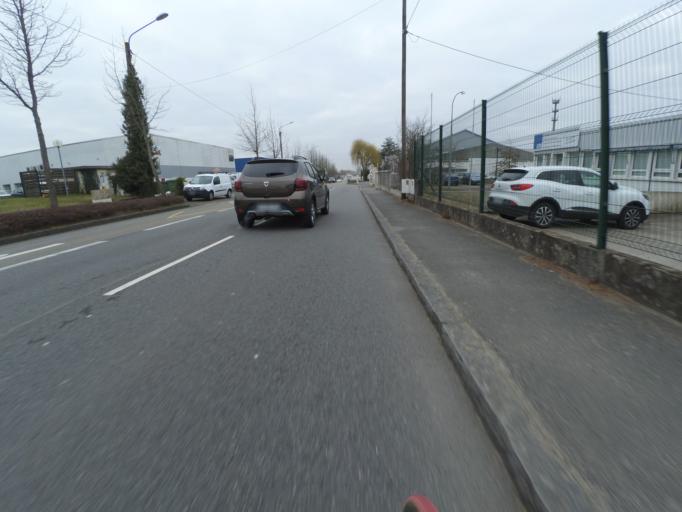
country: FR
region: Pays de la Loire
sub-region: Departement de la Loire-Atlantique
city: Sainte-Luce-sur-Loire
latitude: 47.2661
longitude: -1.4906
